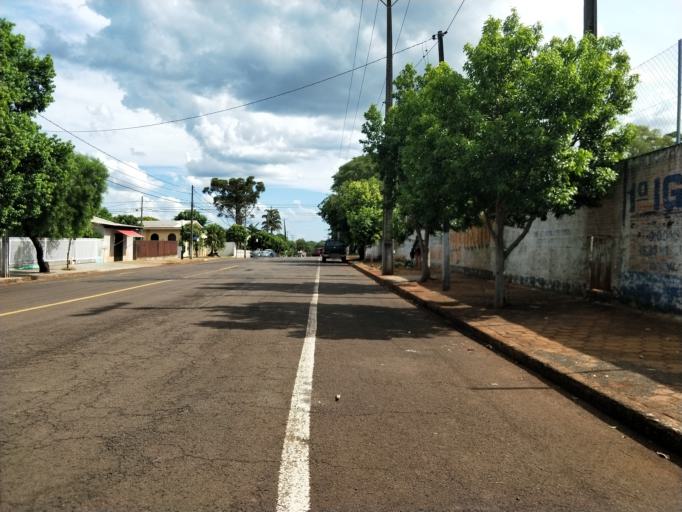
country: BR
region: Parana
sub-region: Marechal Candido Rondon
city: Marechal Candido Rondon
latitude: -24.5613
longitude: -54.0545
